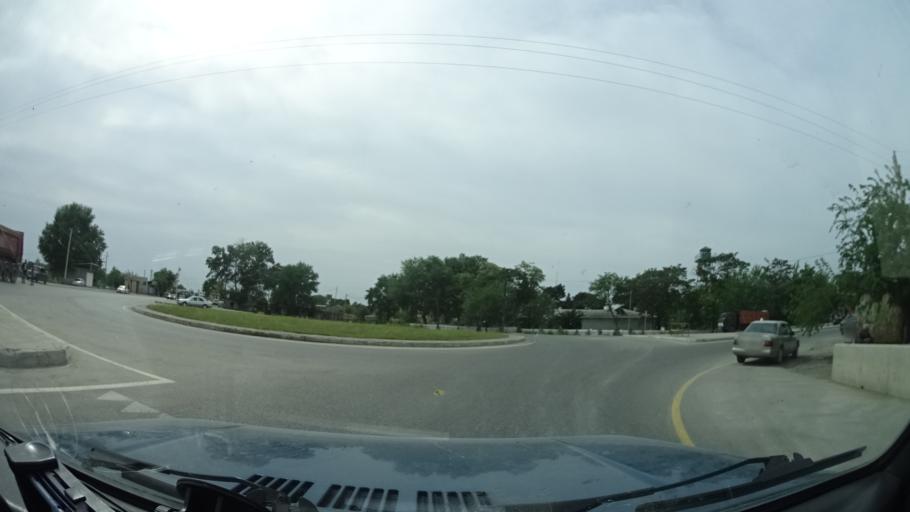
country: IR
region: Ardabil
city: Parsabad
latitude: 39.7354
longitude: 47.9541
